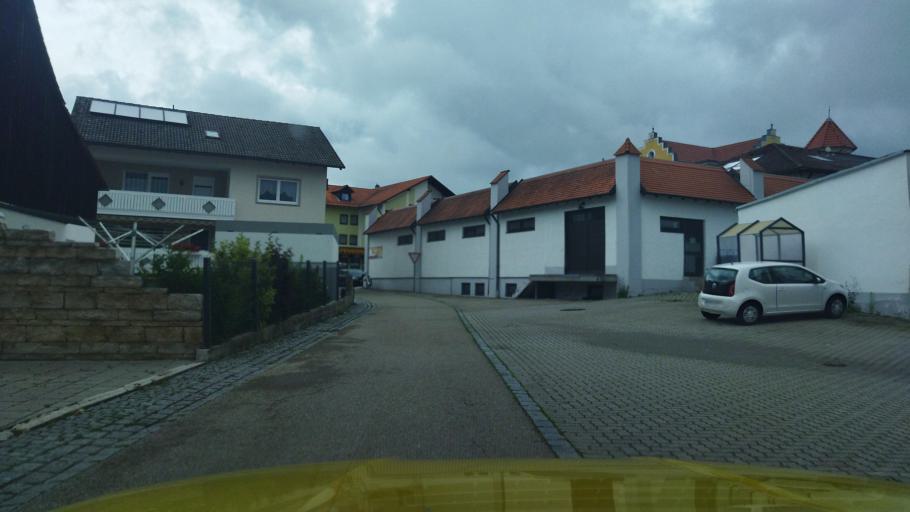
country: DE
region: Bavaria
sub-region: Upper Bavaria
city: Denkendorf
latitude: 48.9275
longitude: 11.4573
